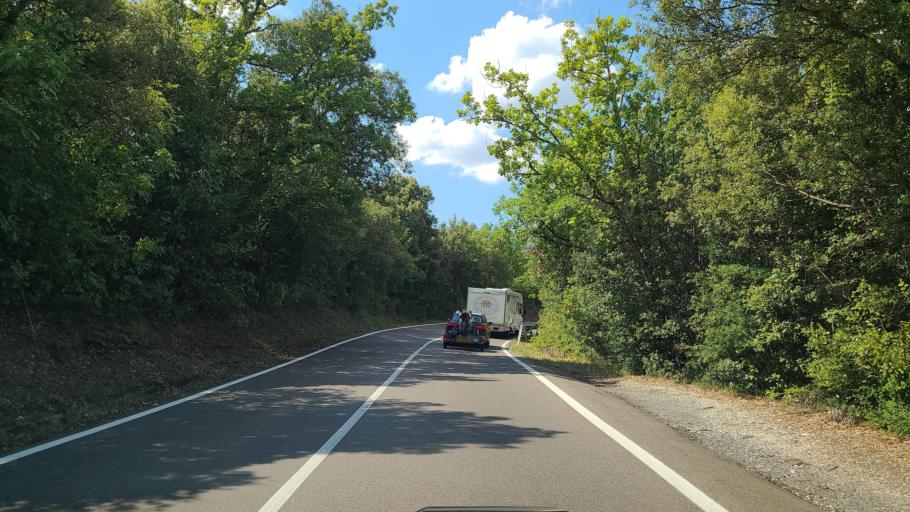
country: IT
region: Tuscany
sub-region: Provincia di Siena
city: Casole d'Elsa
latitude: 43.4015
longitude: 10.9977
